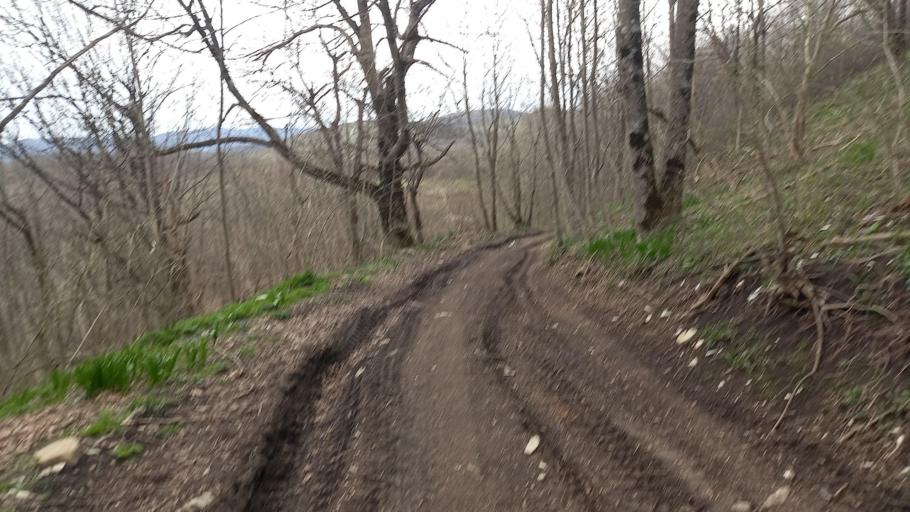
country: RU
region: Krasnodarskiy
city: Divnomorskoye
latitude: 44.6155
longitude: 38.2133
